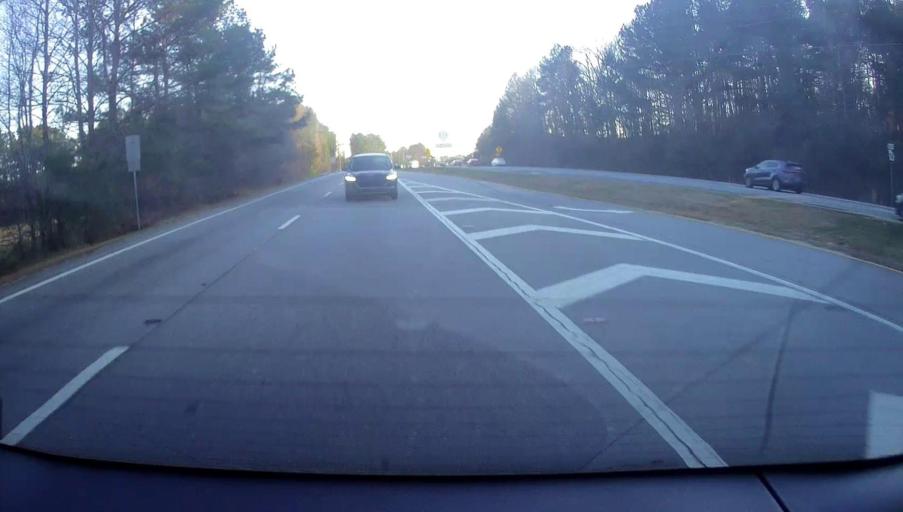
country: US
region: Georgia
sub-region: Fayette County
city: Tyrone
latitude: 33.5107
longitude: -84.5764
